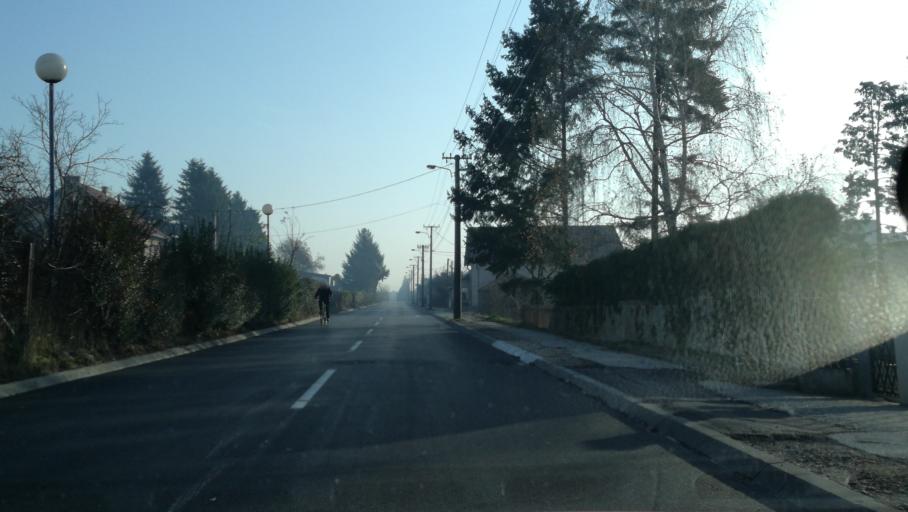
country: RS
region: Central Serbia
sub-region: Moravicki Okrug
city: Cacak
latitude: 43.9020
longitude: 20.3617
